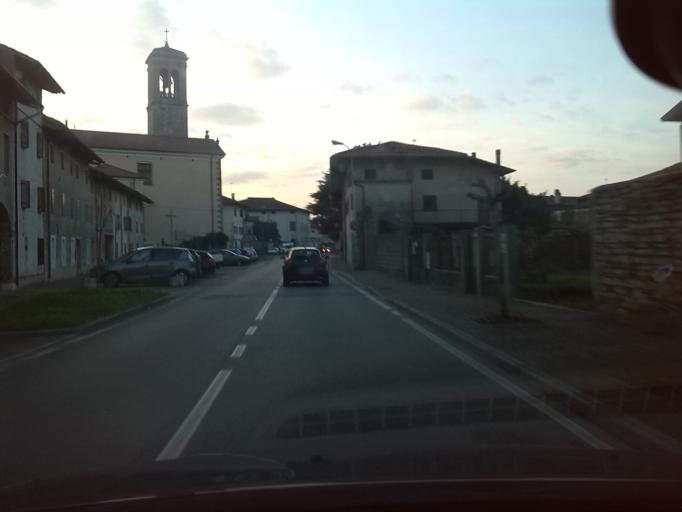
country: IT
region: Friuli Venezia Giulia
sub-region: Provincia di Udine
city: Zugliano-Terenzano-Cargnacco
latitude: 46.0163
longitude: 13.2095
